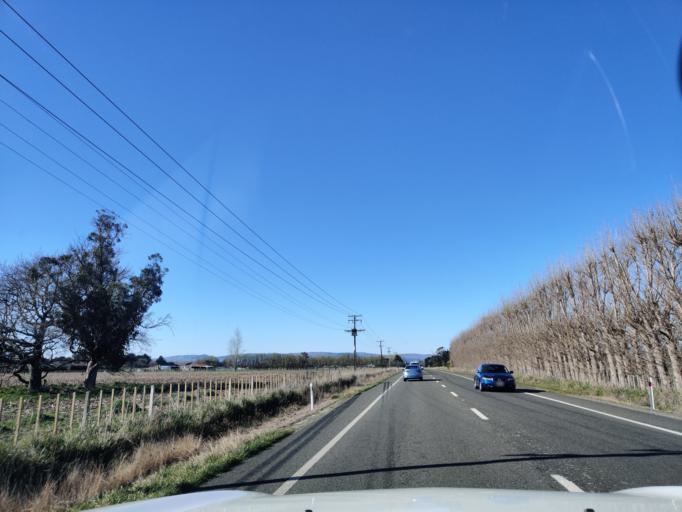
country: NZ
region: Manawatu-Wanganui
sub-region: Palmerston North City
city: Palmerston North
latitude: -40.2995
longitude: 175.5779
